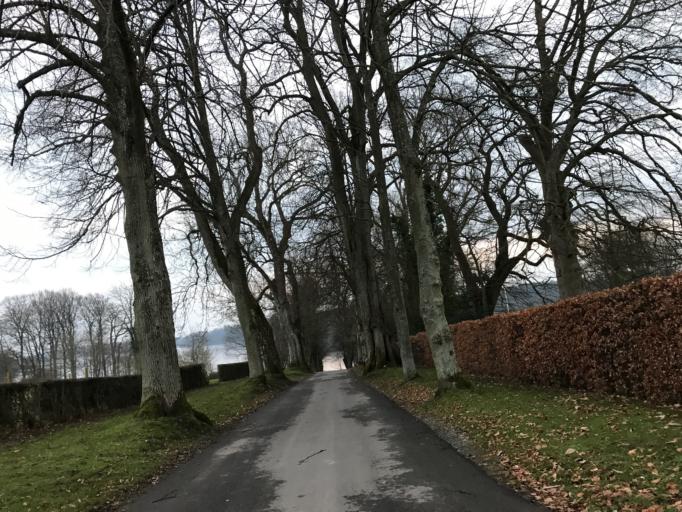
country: DK
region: South Denmark
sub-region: Fredericia Kommune
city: Snoghoj
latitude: 55.5044
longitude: 9.6903
